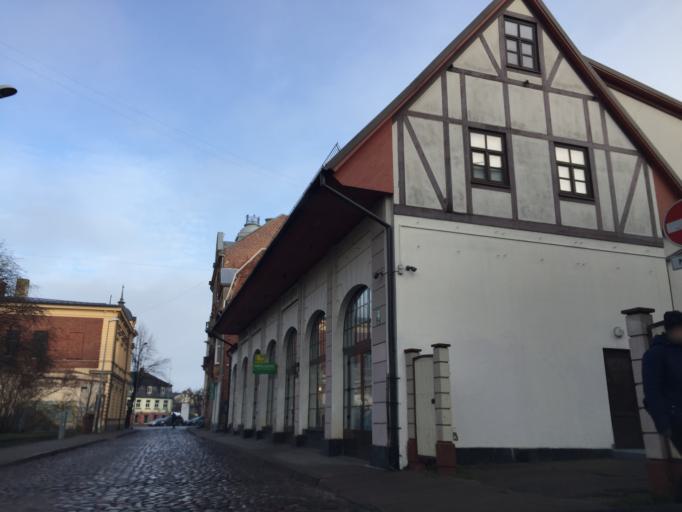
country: LV
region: Liepaja
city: Liepaja
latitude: 56.5086
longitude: 21.0074
